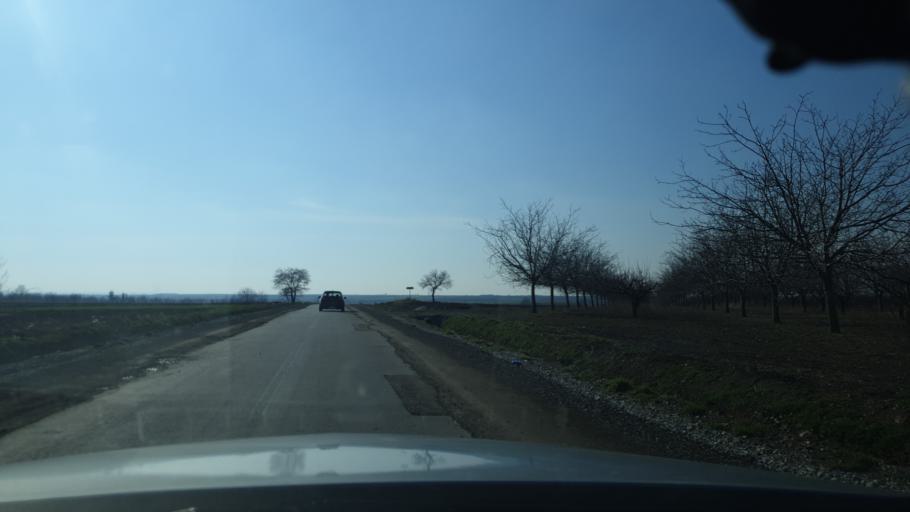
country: RS
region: Autonomna Pokrajina Vojvodina
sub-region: Sremski Okrug
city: Irig
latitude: 45.0818
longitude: 19.8462
